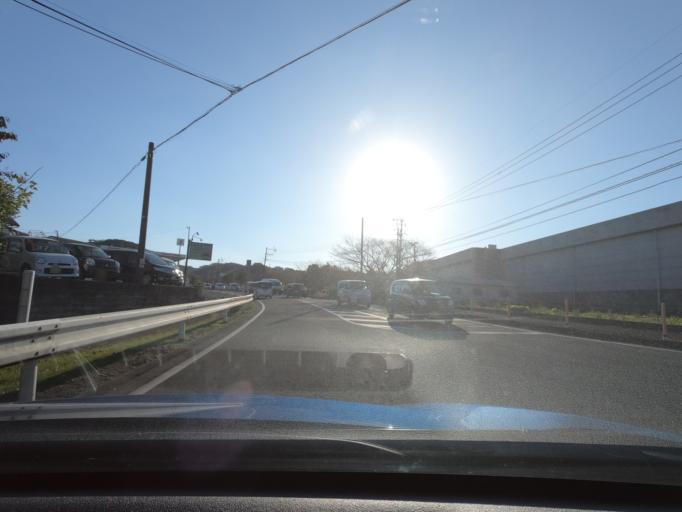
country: JP
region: Kagoshima
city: Akune
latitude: 32.0597
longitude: 130.2227
